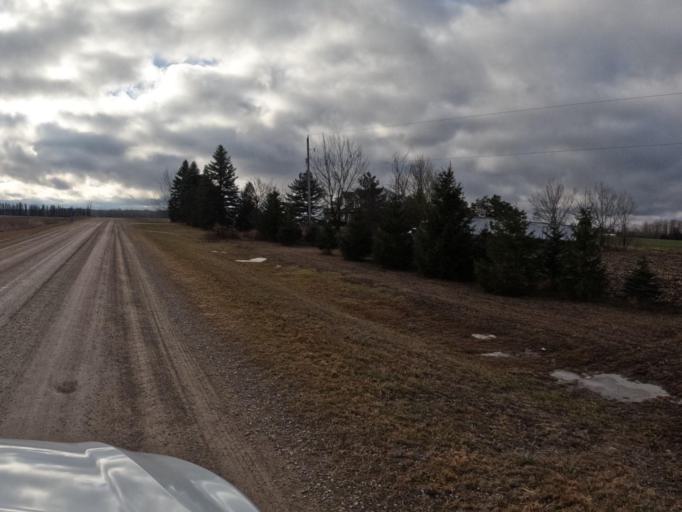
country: CA
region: Ontario
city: Shelburne
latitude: 43.8719
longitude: -80.3560
